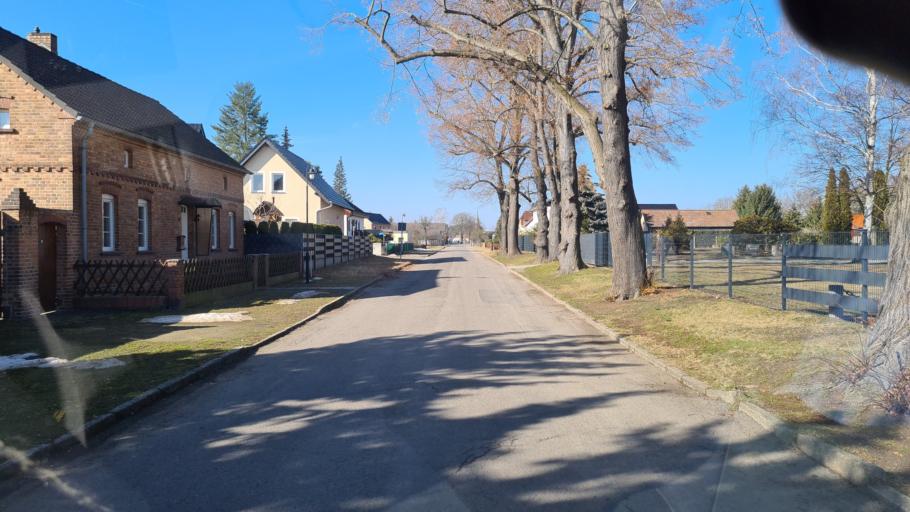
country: DE
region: Brandenburg
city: Senftenberg
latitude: 51.4934
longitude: 14.0680
